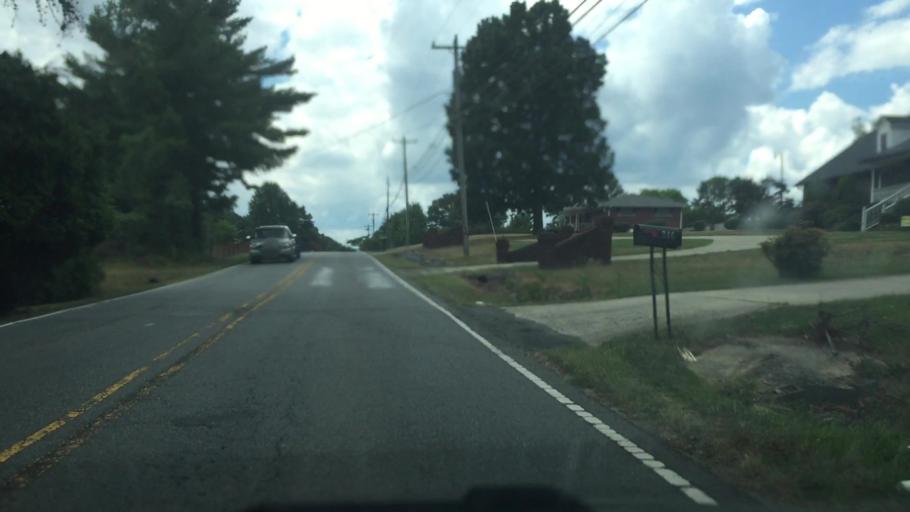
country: US
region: North Carolina
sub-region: Rowan County
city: Enochville
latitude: 35.5116
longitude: -80.6721
